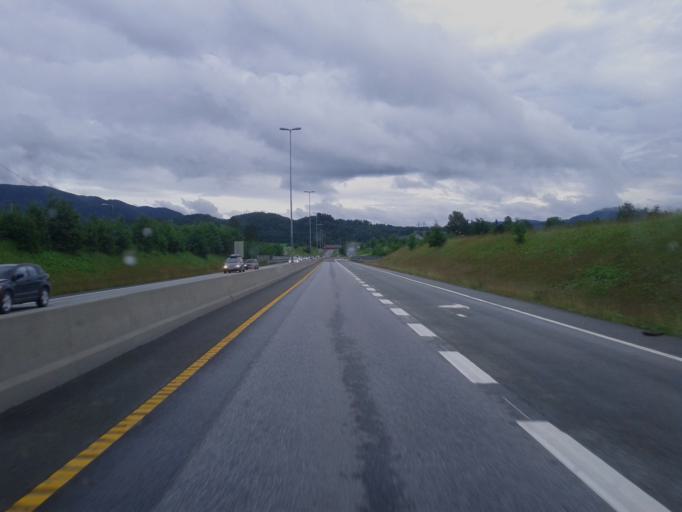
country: NO
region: Sor-Trondelag
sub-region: Melhus
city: Melhus
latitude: 63.3044
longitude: 10.2882
